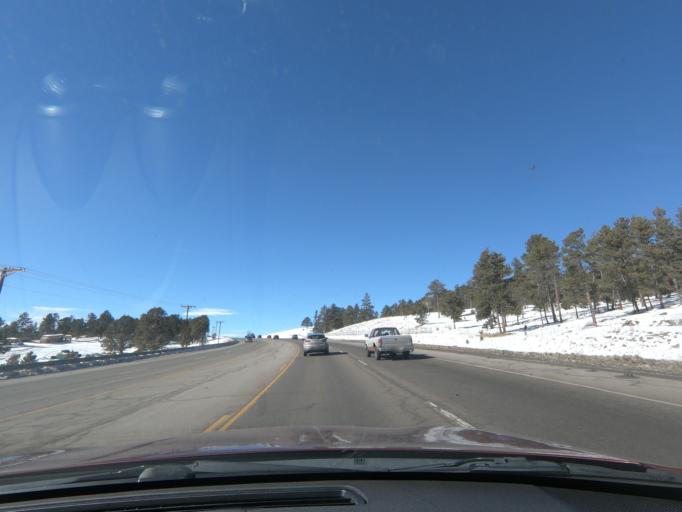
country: US
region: Colorado
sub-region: Teller County
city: Woodland Park
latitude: 38.9580
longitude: -105.1101
